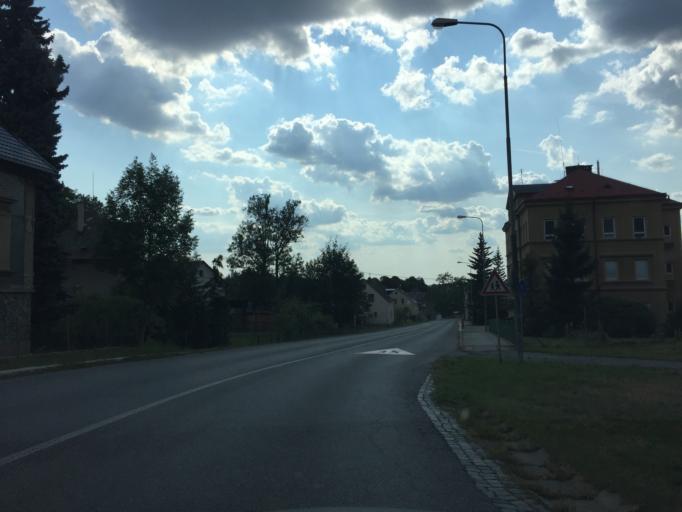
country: CZ
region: Liberecky
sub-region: Okres Jablonec nad Nisou
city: Jablonec nad Nisou
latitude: 50.7014
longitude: 15.1815
